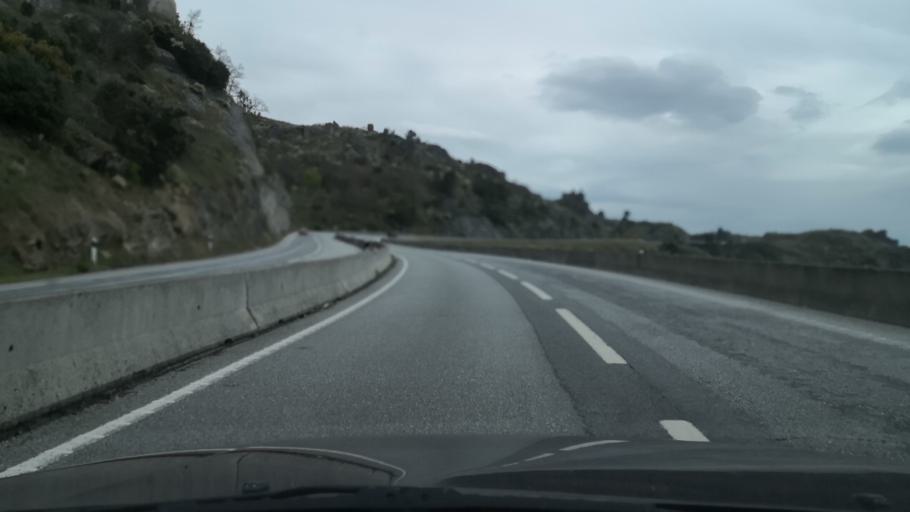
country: PT
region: Guarda
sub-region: Guarda
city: Guarda
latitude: 40.5955
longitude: -7.2758
